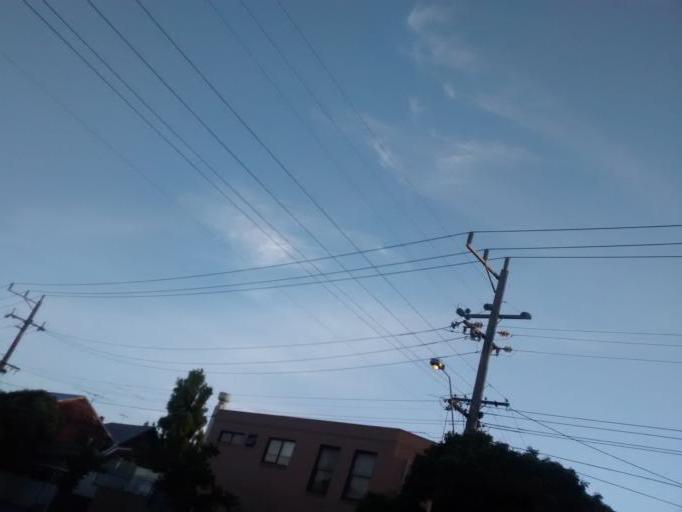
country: AU
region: Victoria
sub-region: Port Phillip
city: Port Melbourne
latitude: -37.8337
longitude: 144.9469
